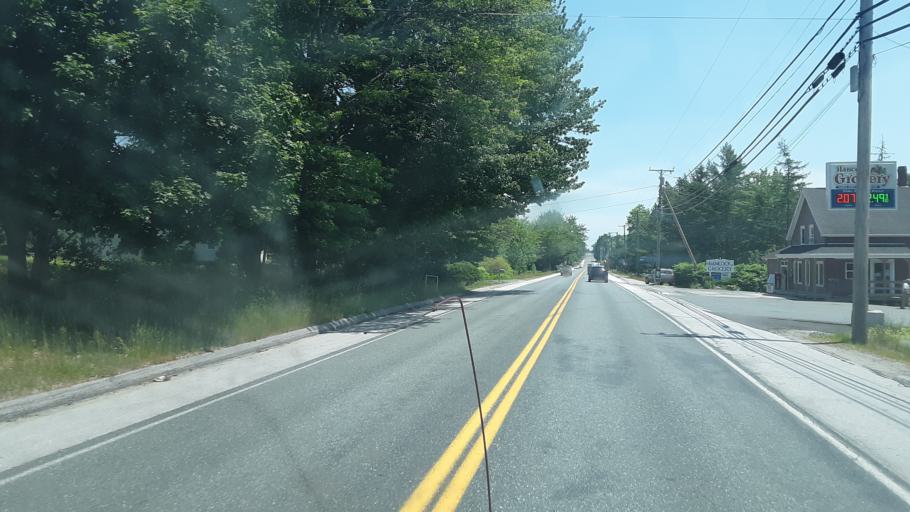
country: US
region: Maine
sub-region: Hancock County
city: Hancock
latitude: 44.5305
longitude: -68.2595
